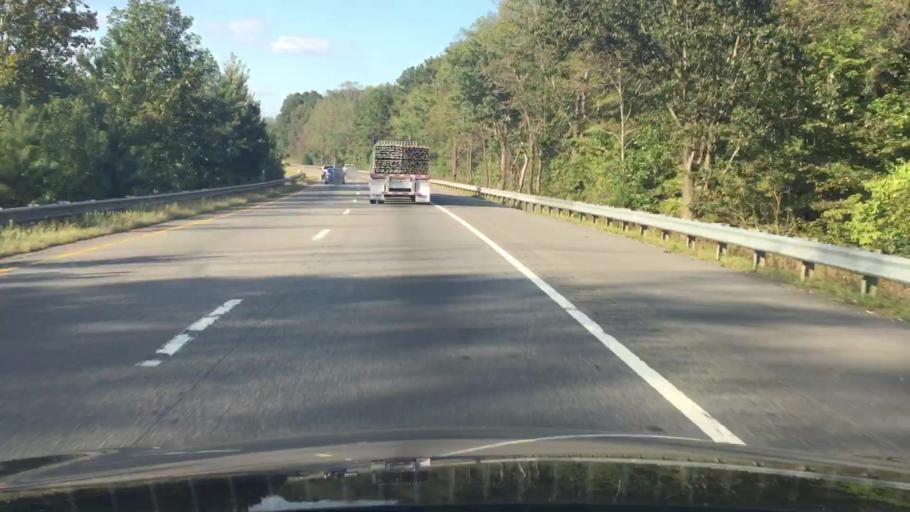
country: US
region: North Carolina
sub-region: Iredell County
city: Troutman
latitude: 35.7106
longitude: -80.8551
